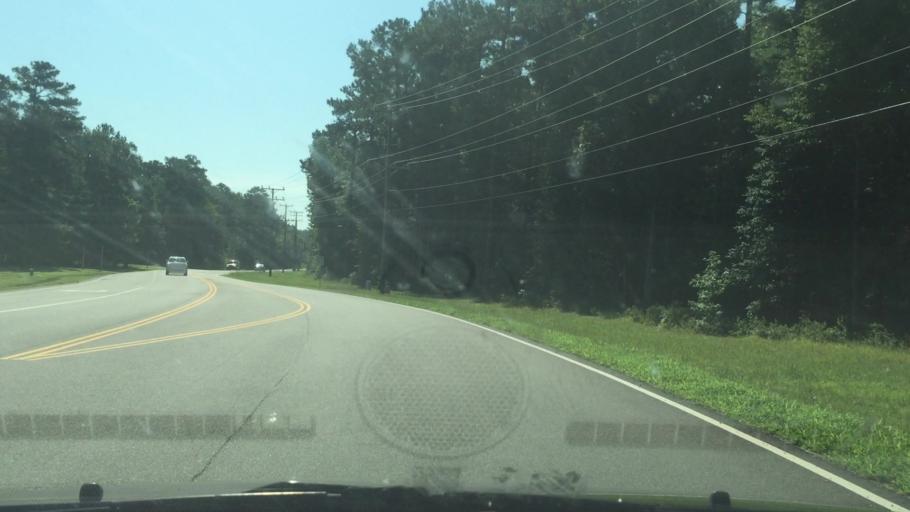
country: US
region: Virginia
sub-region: Hanover County
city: Ashland
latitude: 37.7430
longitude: -77.4670
